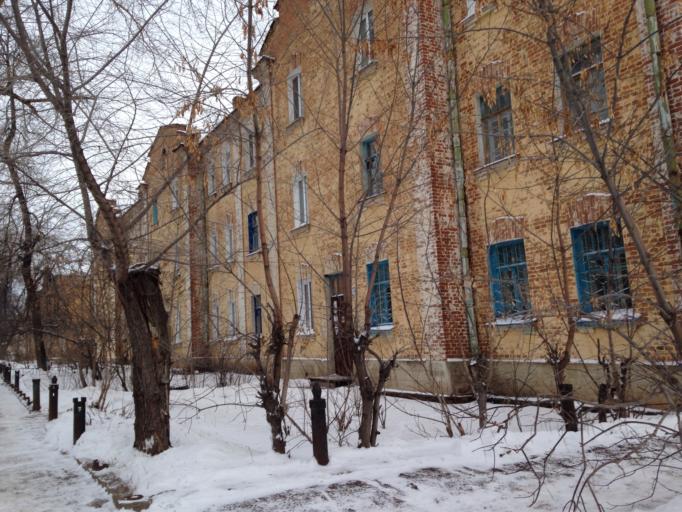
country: RU
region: Ulyanovsk
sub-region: Ulyanovskiy Rayon
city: Ulyanovsk
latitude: 54.3275
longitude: 48.4730
